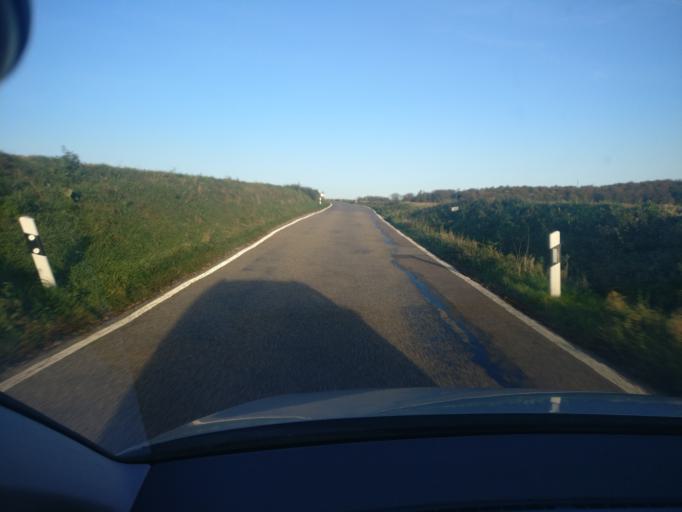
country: DE
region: Baden-Wuerttemberg
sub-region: Karlsruhe Region
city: Joehlingen
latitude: 49.0367
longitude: 8.5965
